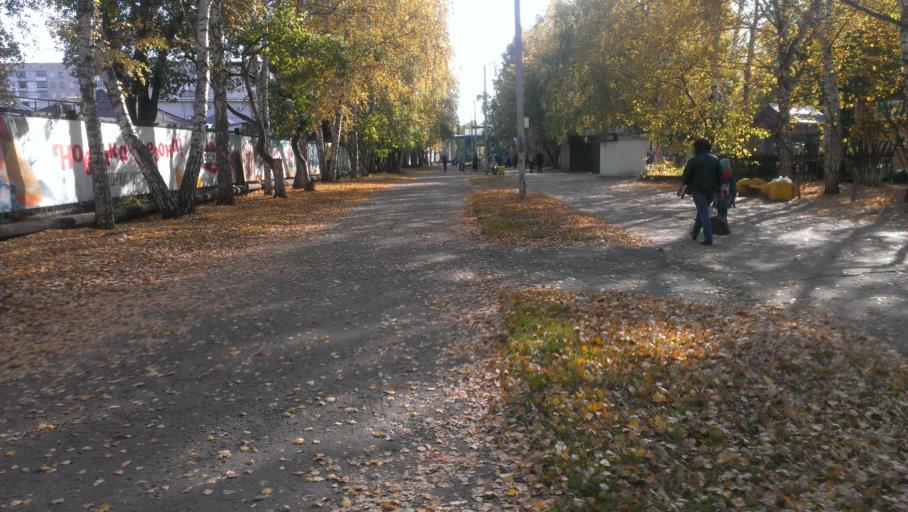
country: RU
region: Altai Krai
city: Novosilikatnyy
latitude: 53.3564
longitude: 83.6846
